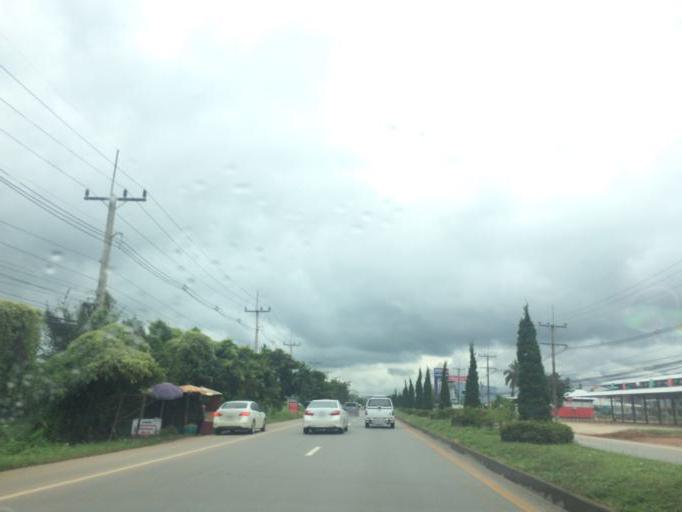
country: TH
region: Chiang Rai
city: Chiang Rai
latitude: 20.0184
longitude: 99.8703
